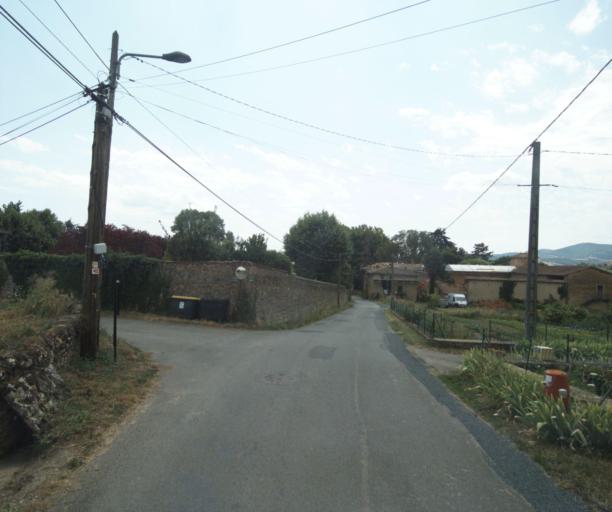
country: FR
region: Rhone-Alpes
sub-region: Departement du Rhone
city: Saint-Germain-Nuelles
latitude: 45.8591
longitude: 4.5999
